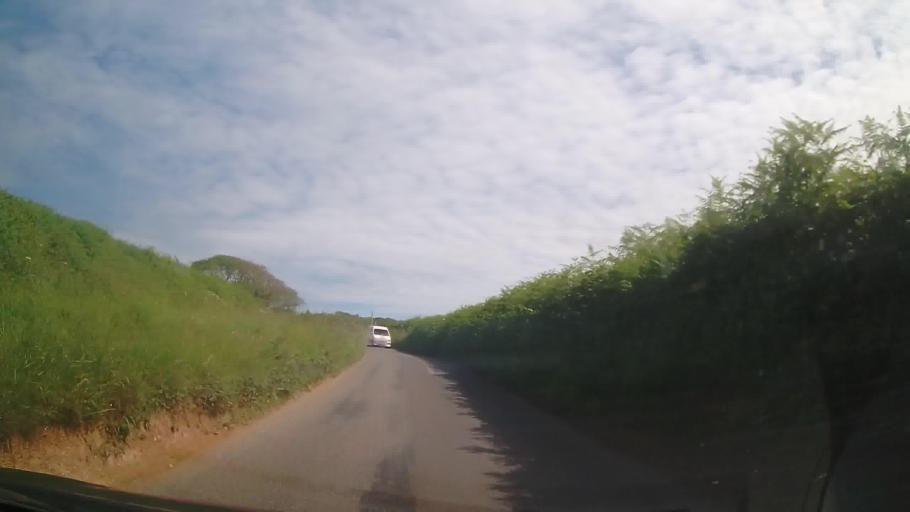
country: GB
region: England
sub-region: Devon
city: Salcombe
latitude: 50.2676
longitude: -3.6776
